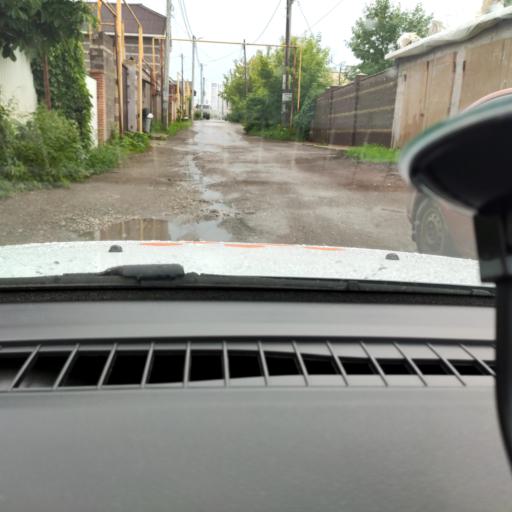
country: RU
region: Samara
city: Samara
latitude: 53.2710
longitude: 50.2174
